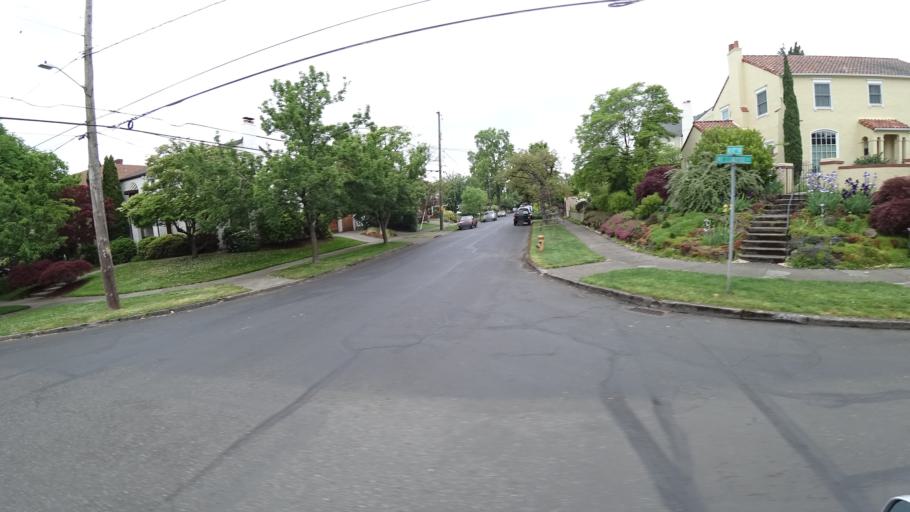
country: US
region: Oregon
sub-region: Multnomah County
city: Portland
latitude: 45.5454
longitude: -122.6197
